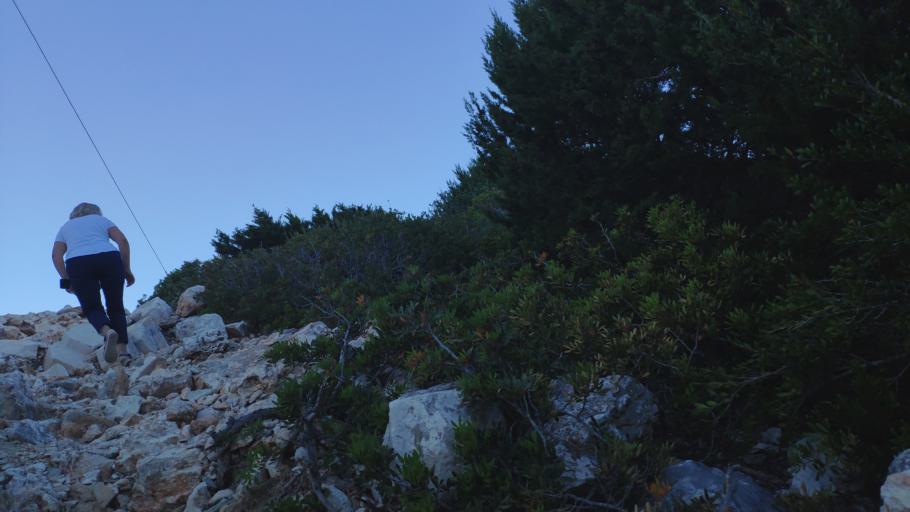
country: GR
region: Ionian Islands
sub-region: Lefkada
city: Nidri
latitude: 38.5634
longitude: 20.5427
